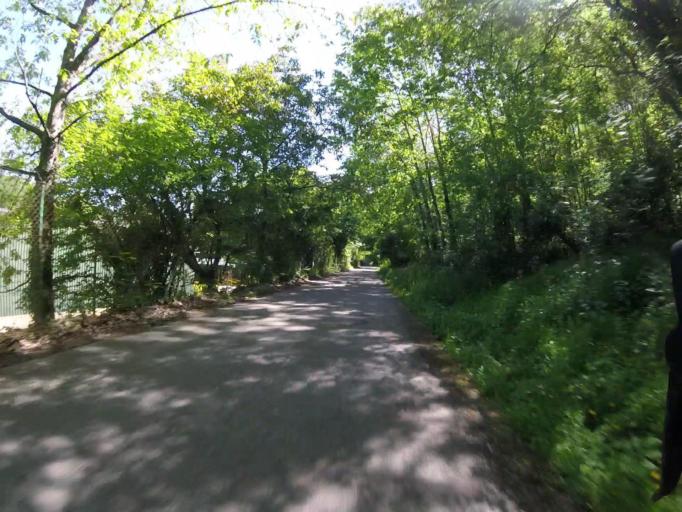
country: ES
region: Navarre
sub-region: Provincia de Navarra
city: Bera
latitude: 43.2747
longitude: -1.7037
